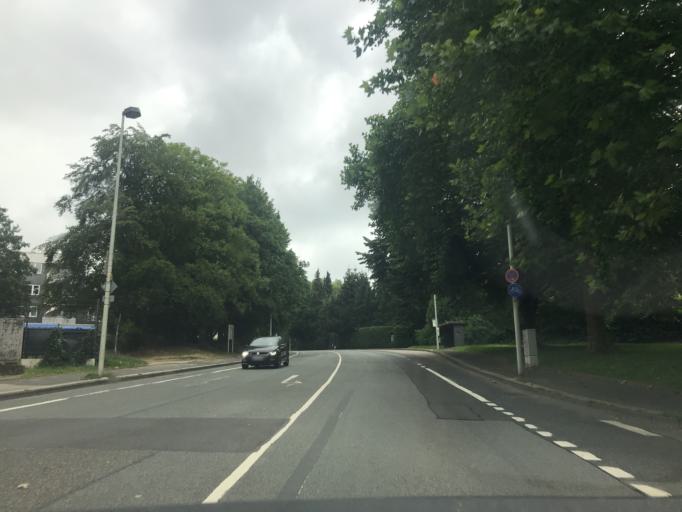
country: DE
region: North Rhine-Westphalia
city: Haan
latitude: 51.1787
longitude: 7.0173
